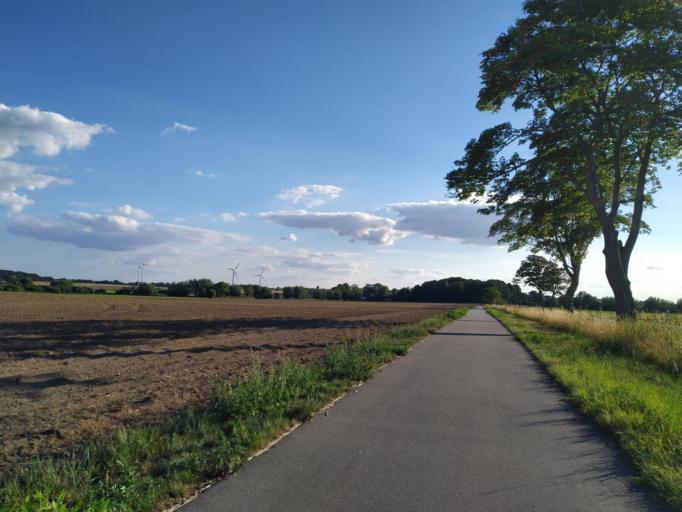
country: DE
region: Mecklenburg-Vorpommern
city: Kalkhorst
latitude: 53.9642
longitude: 11.0287
